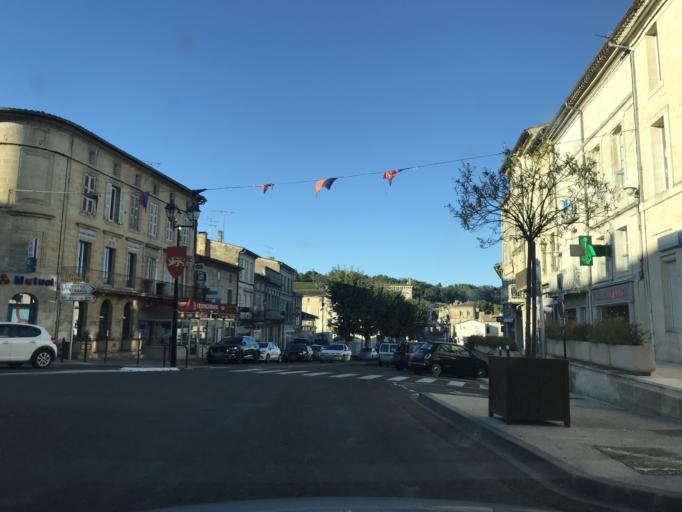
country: FR
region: Aquitaine
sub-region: Departement de la Gironde
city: Mouliets-et-Villemartin
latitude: 44.8532
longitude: -0.0432
